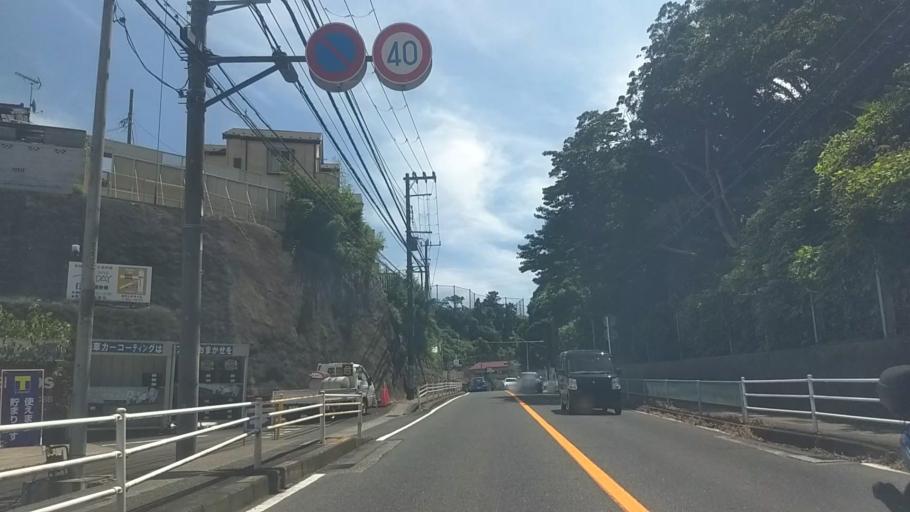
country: JP
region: Kanagawa
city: Yokosuka
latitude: 35.2481
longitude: 139.6651
